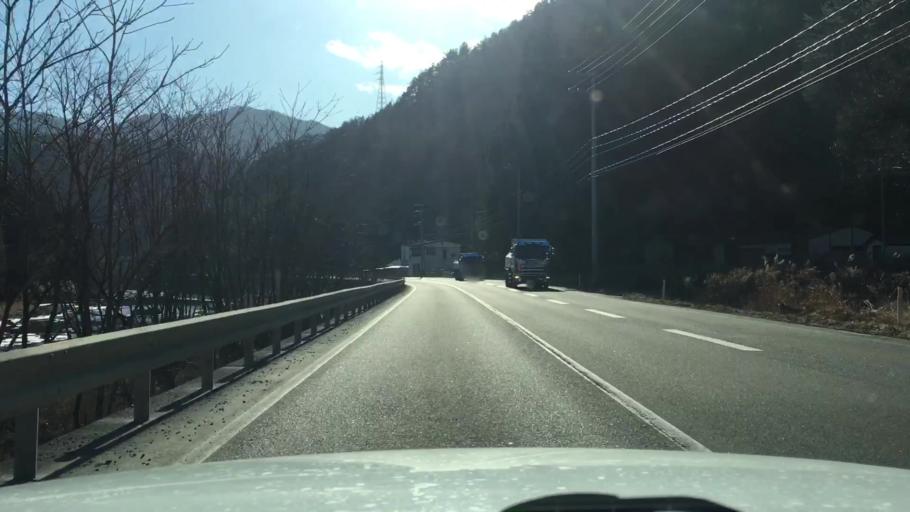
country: JP
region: Iwate
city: Miyako
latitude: 39.6163
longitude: 141.7895
